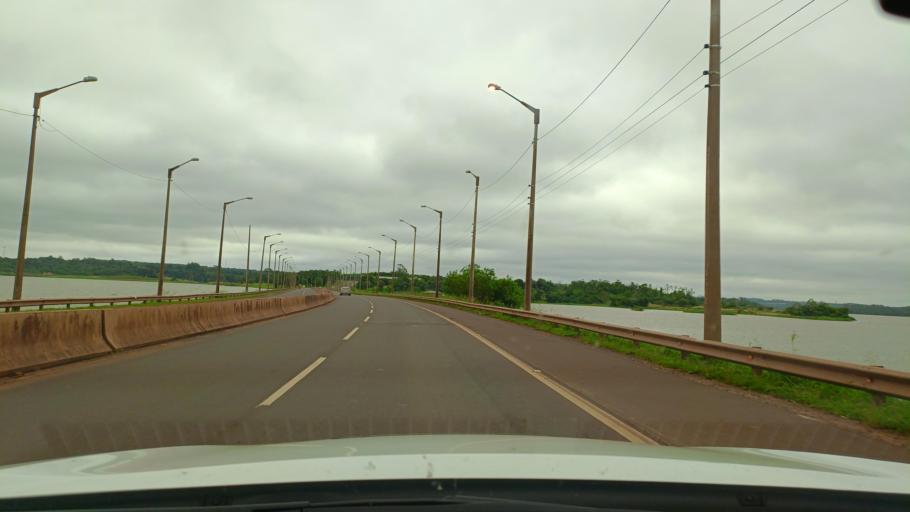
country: PY
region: Itapua
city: Encarnacion
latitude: -27.2959
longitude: -55.9036
